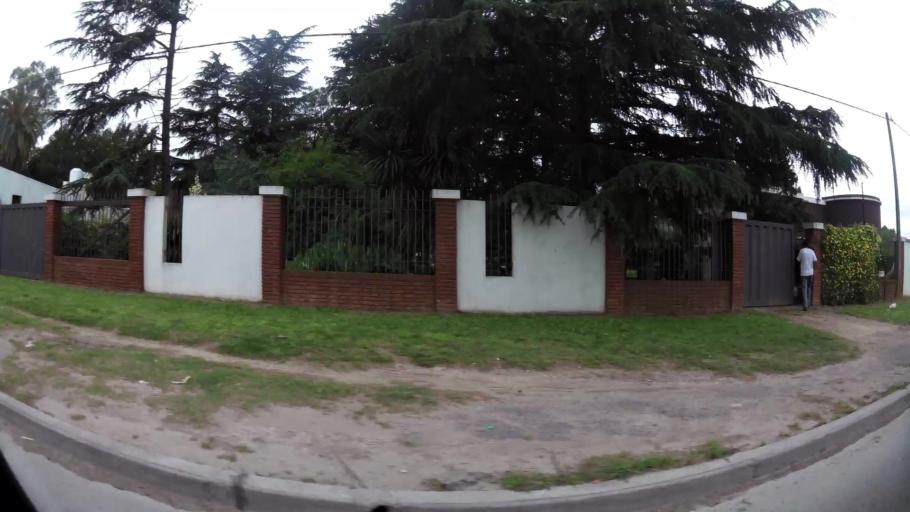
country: AR
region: Buenos Aires
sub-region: Partido de La Plata
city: La Plata
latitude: -34.9687
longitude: -58.0189
